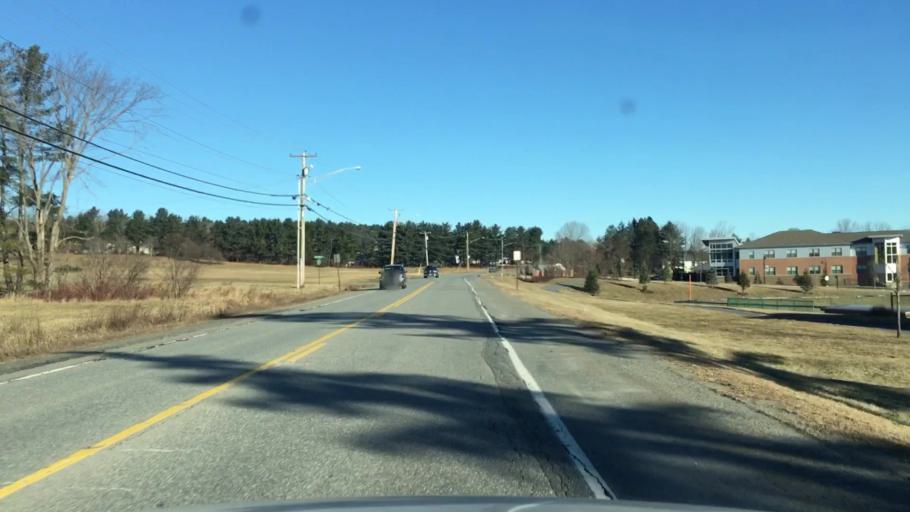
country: US
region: Maine
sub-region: Kennebec County
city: Waterville
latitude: 44.5243
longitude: -69.6666
